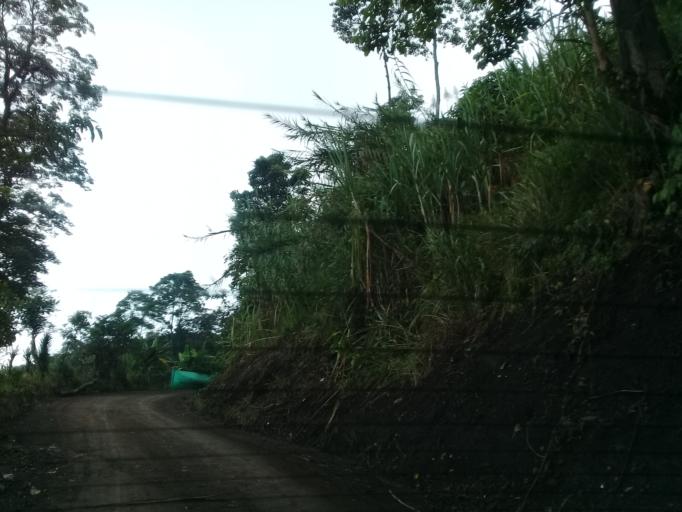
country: CO
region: Cundinamarca
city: Quipile
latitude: 4.7424
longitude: -74.5333
